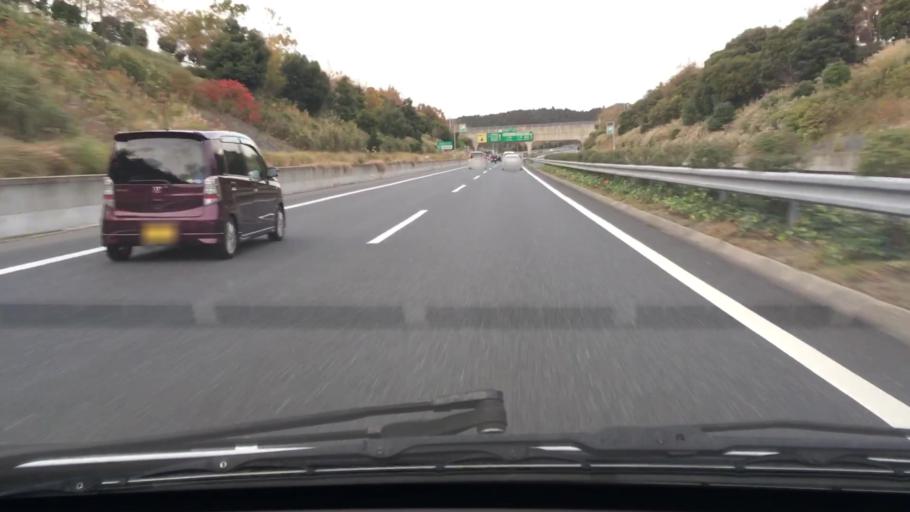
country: JP
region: Chiba
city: Kisarazu
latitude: 35.3434
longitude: 139.9442
